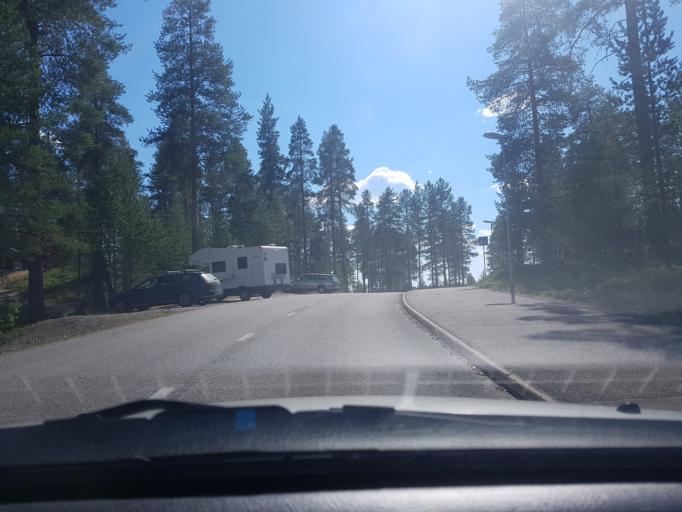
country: FI
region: Kainuu
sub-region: Kehys-Kainuu
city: Kuhmo
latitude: 64.1172
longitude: 29.5870
